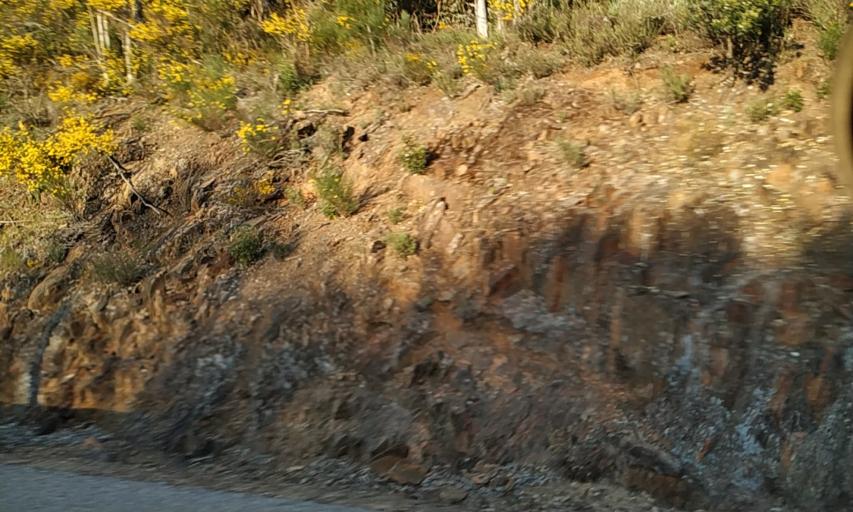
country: PT
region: Portalegre
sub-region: Portalegre
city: Sao Juliao
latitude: 39.3450
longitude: -7.2757
